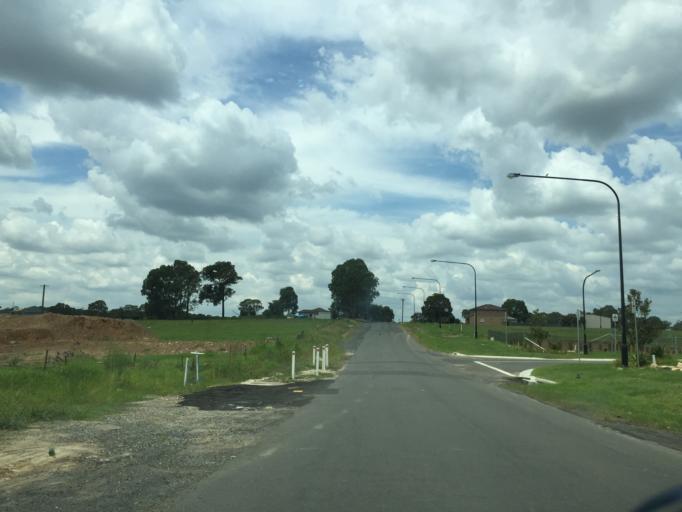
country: AU
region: New South Wales
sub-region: Blacktown
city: Riverstone
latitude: -33.6982
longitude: 150.8875
